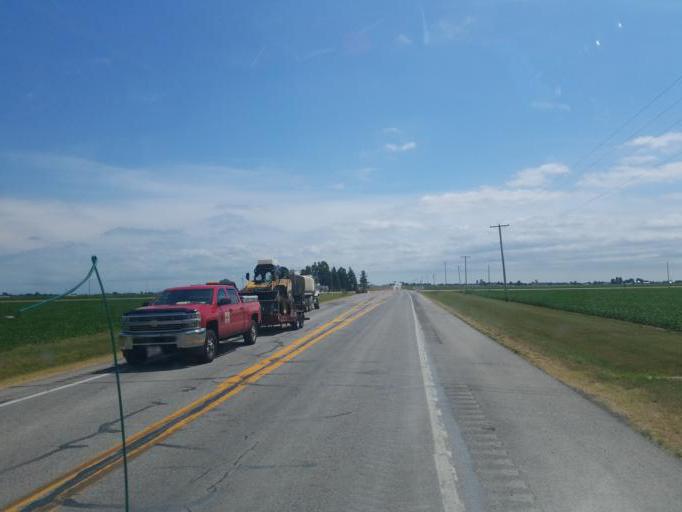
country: US
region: Indiana
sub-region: Allen County
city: Woodburn
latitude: 41.1563
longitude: -84.8488
